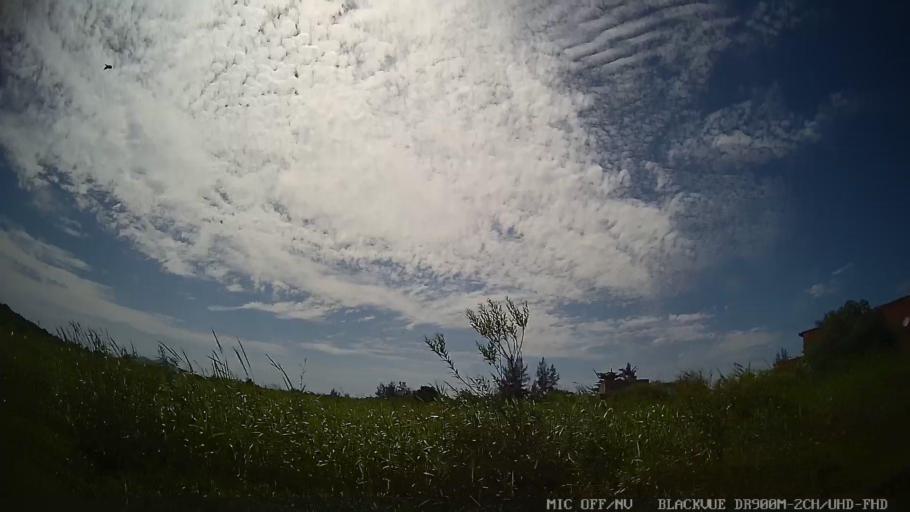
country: BR
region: Sao Paulo
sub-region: Iguape
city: Iguape
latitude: -24.7893
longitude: -47.6183
